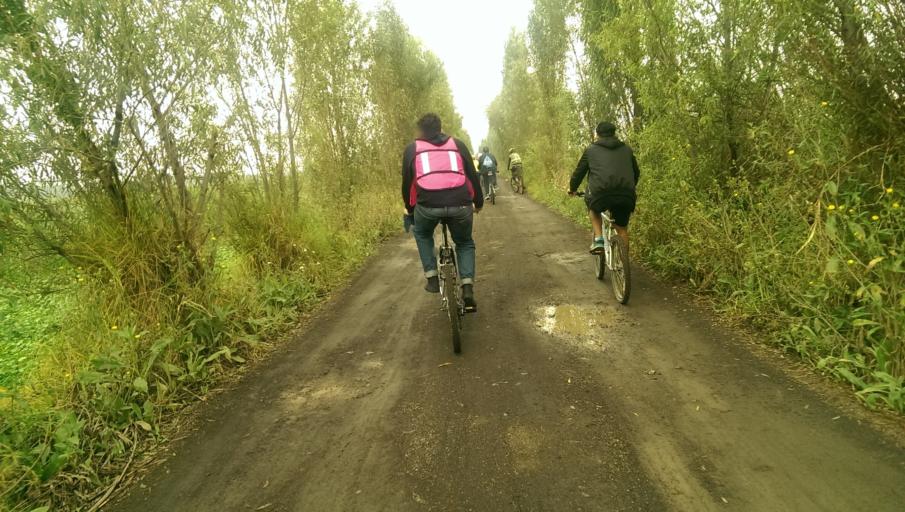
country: MX
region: Mexico City
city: Tlahuac
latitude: 19.2656
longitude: -99.0523
